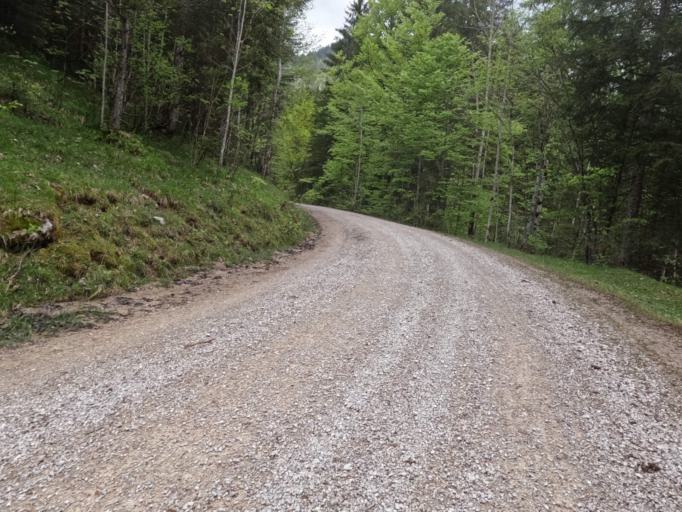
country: AT
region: Salzburg
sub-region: Politischer Bezirk Zell am See
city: Unken
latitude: 47.7142
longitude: 12.6943
